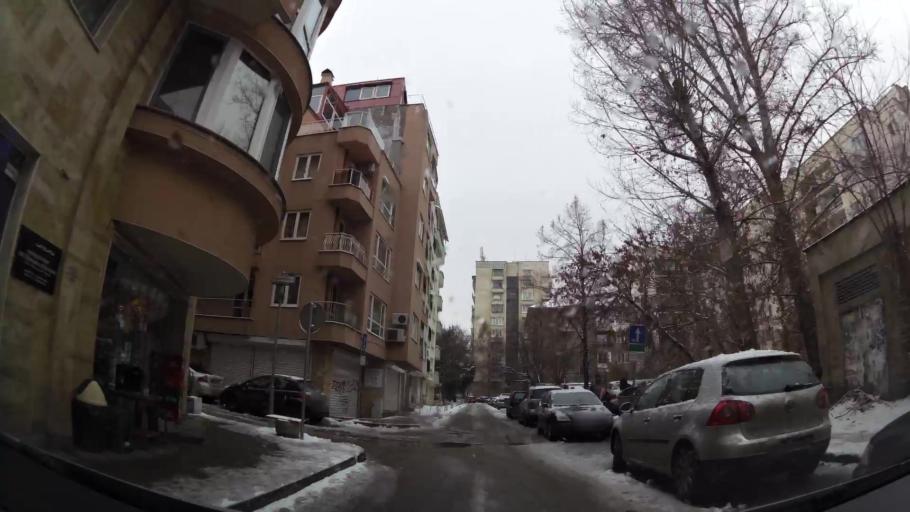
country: BG
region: Sofia-Capital
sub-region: Stolichna Obshtina
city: Sofia
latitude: 42.6929
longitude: 23.3521
